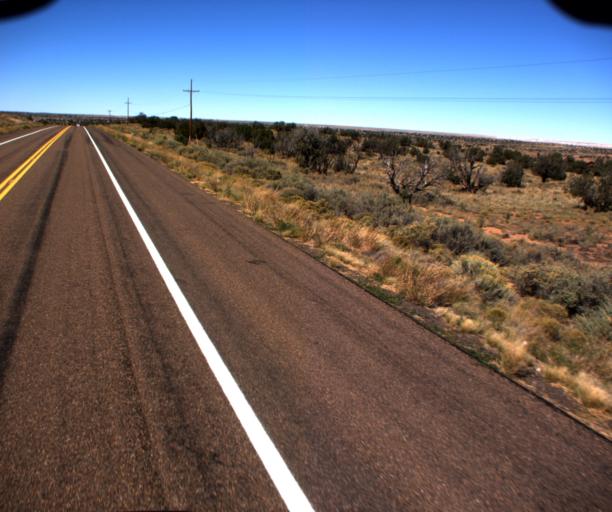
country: US
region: Arizona
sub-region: Apache County
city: Saint Johns
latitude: 34.6390
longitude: -109.6906
